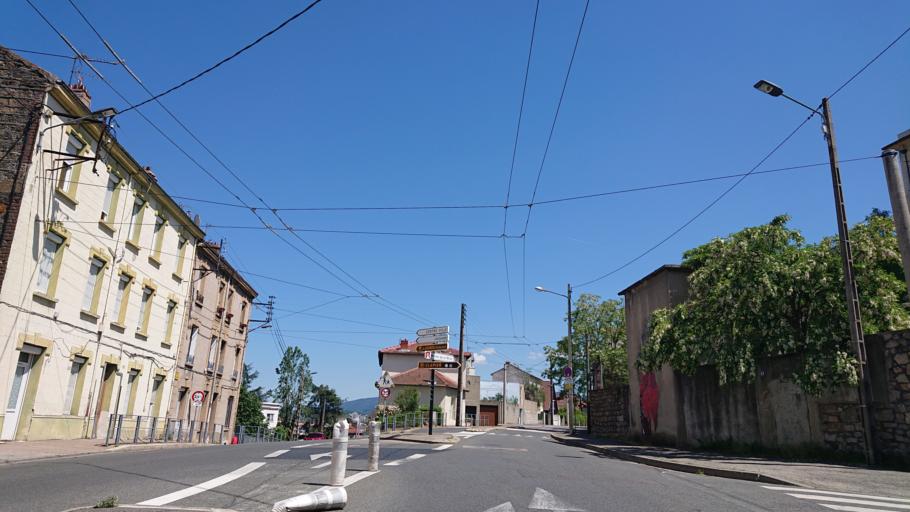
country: FR
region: Rhone-Alpes
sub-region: Departement de la Loire
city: Saint-Etienne
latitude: 45.4426
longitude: 4.3730
